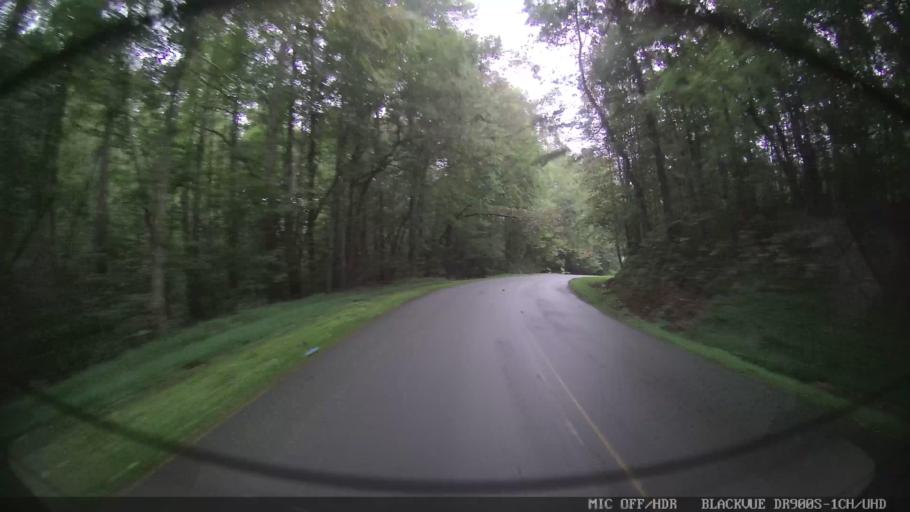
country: US
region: Georgia
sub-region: Gilmer County
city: Ellijay
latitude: 34.7591
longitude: -84.5314
